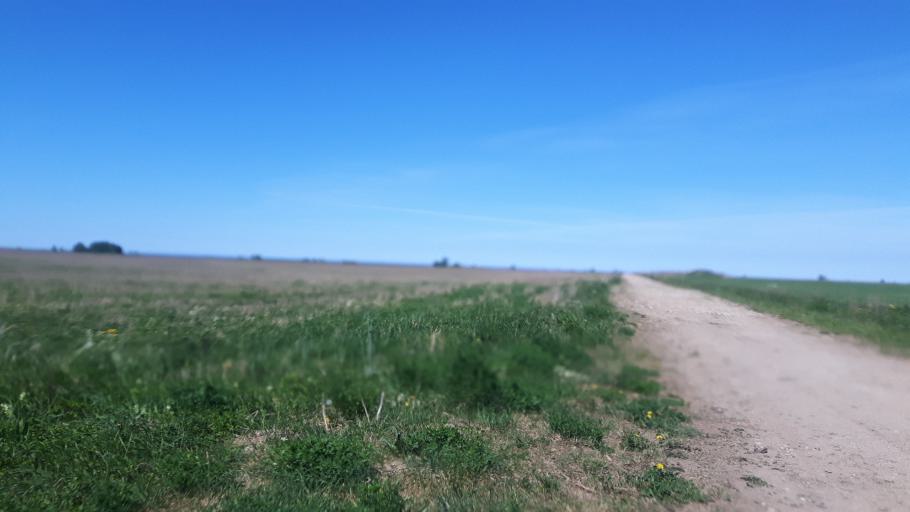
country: EE
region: Ida-Virumaa
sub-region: Toila vald
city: Voka
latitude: 59.4095
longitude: 27.6467
